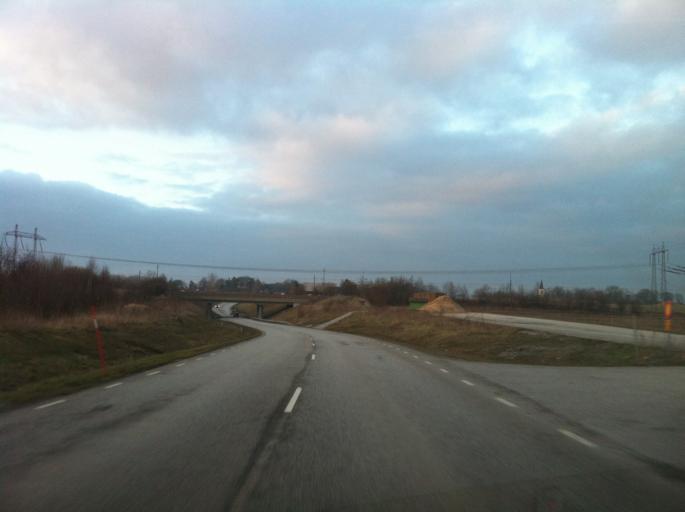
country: SE
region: Skane
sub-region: Kavlinge Kommun
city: Kaevlinge
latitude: 55.8137
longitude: 13.0918
